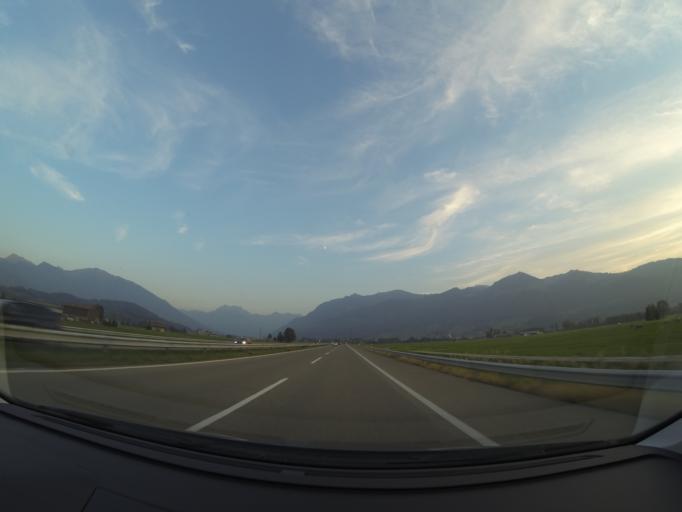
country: CH
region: Schwyz
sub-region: Bezirk March
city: Tuggen
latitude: 47.1949
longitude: 8.9718
